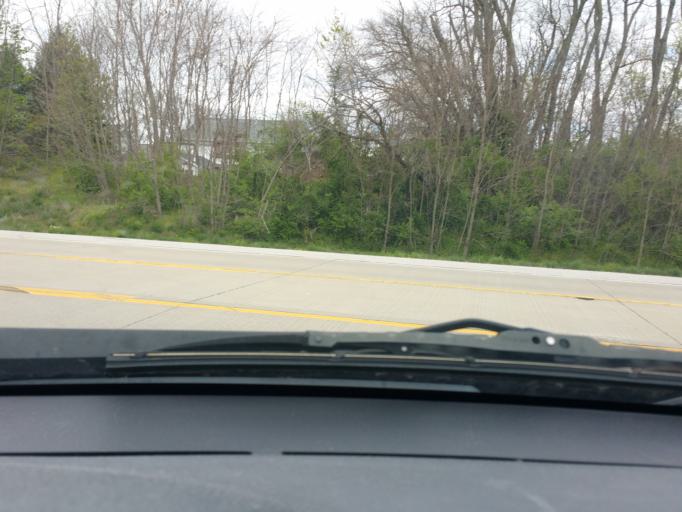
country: US
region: Illinois
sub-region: Madison County
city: Edwardsville
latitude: 38.7872
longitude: -89.9289
